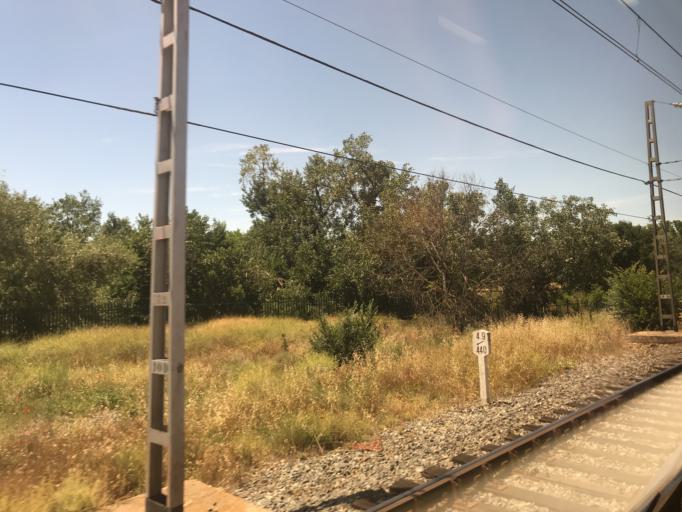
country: ES
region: Madrid
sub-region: Provincia de Madrid
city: Aranjuez
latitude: 40.0393
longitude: -3.6200
